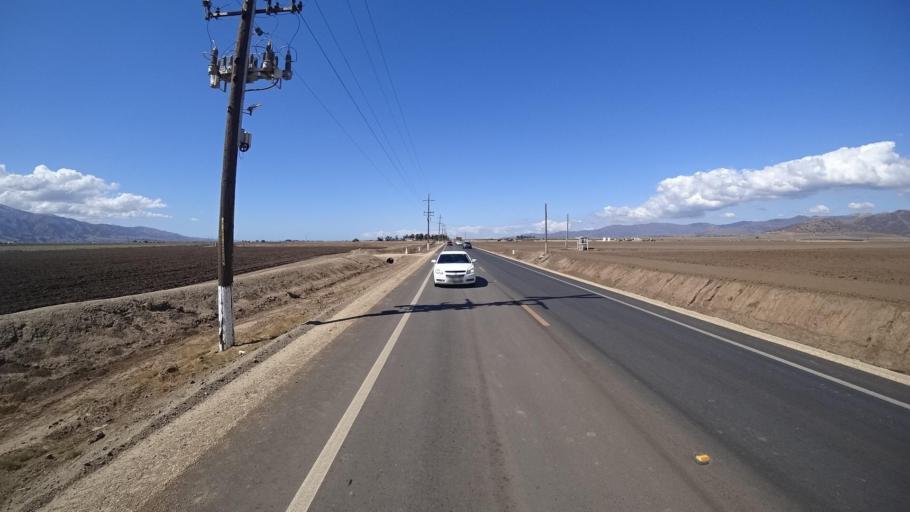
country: US
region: California
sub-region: Monterey County
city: Gonzales
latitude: 36.5407
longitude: -121.4631
